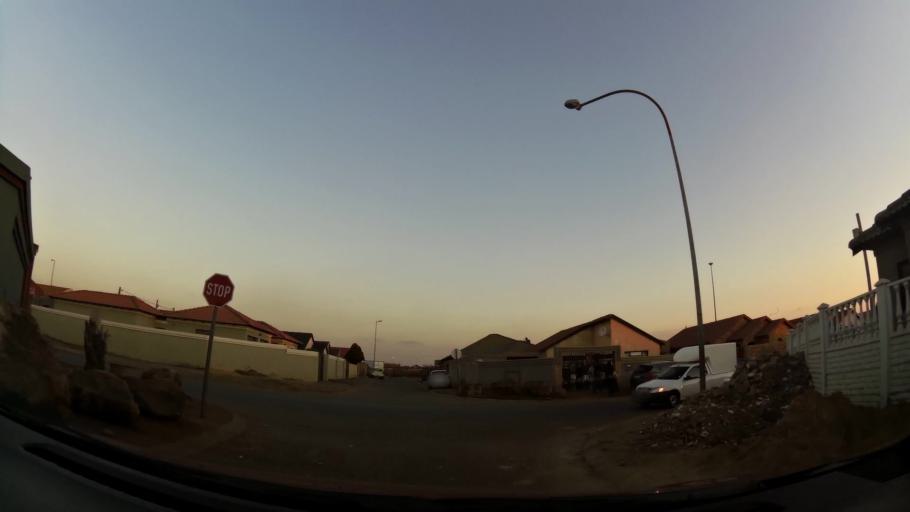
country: ZA
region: Gauteng
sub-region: City of Johannesburg Metropolitan Municipality
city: Soweto
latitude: -26.2278
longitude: 27.8414
